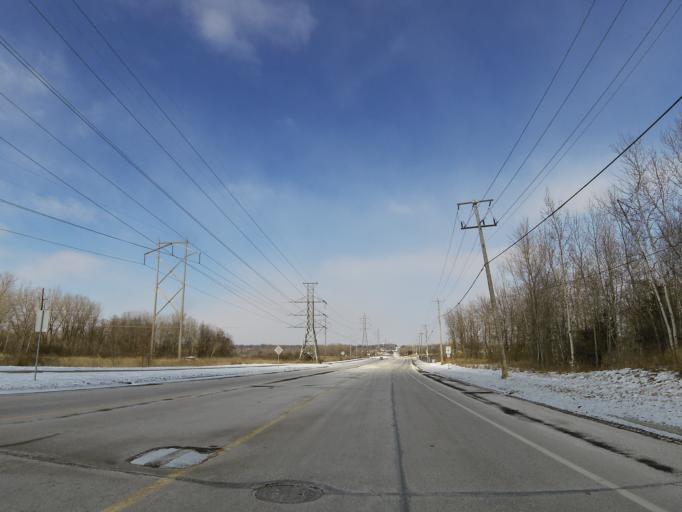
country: US
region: Minnesota
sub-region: Washington County
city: Woodbury
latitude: 44.9331
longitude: -92.9645
